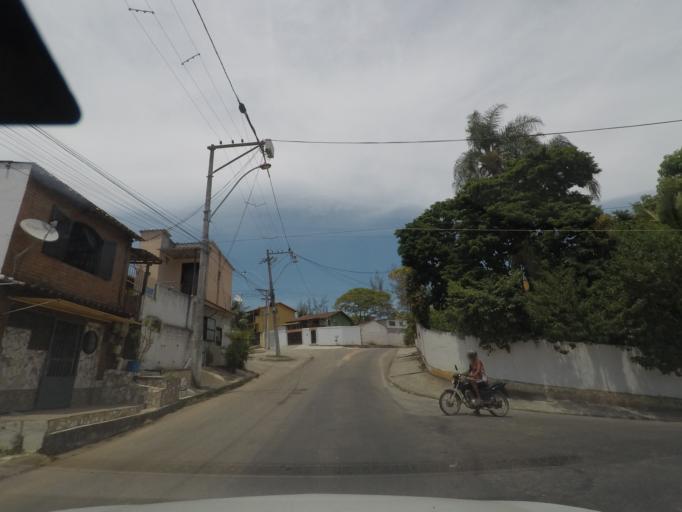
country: BR
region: Rio de Janeiro
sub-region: Marica
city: Marica
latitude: -22.9249
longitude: -42.8179
